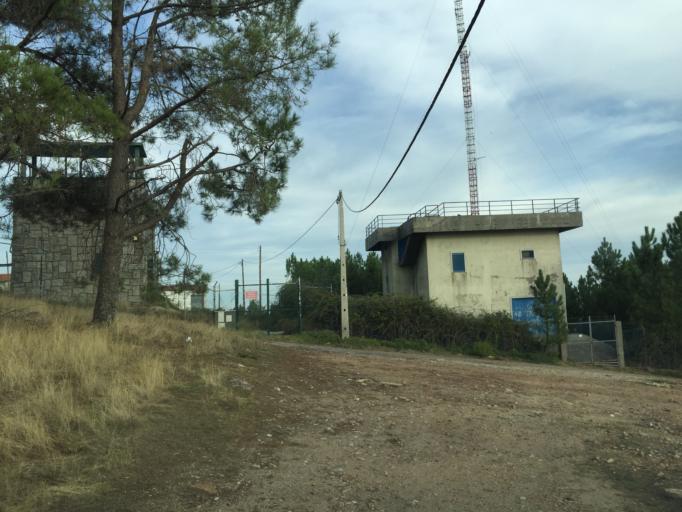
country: PT
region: Portalegre
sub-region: Portalegre
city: Reguengo
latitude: 39.3130
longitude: -7.3600
